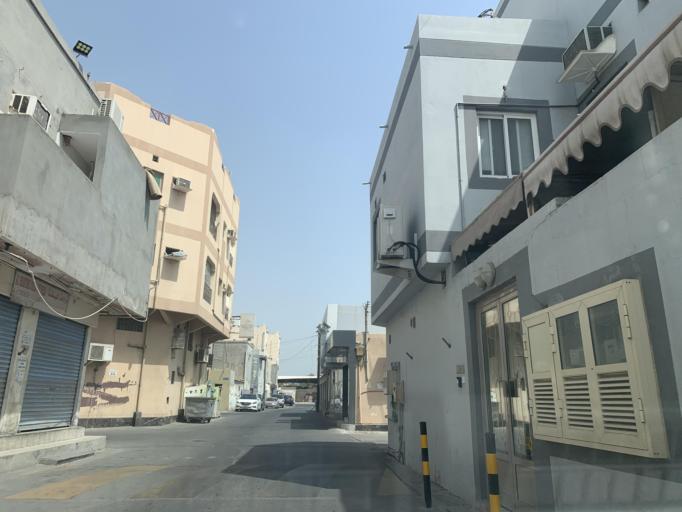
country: BH
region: Northern
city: Madinat `Isa
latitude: 26.1836
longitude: 50.5471
